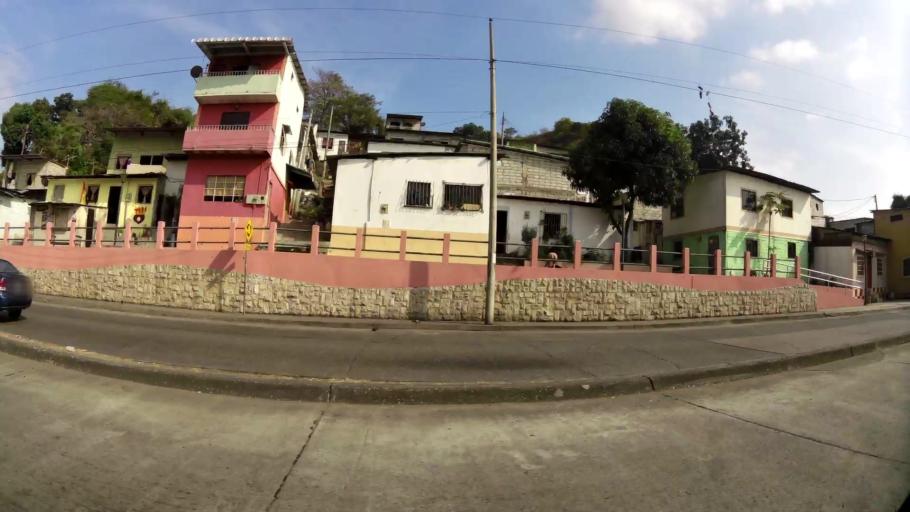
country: EC
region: Guayas
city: Guayaquil
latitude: -2.1866
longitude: -79.9048
